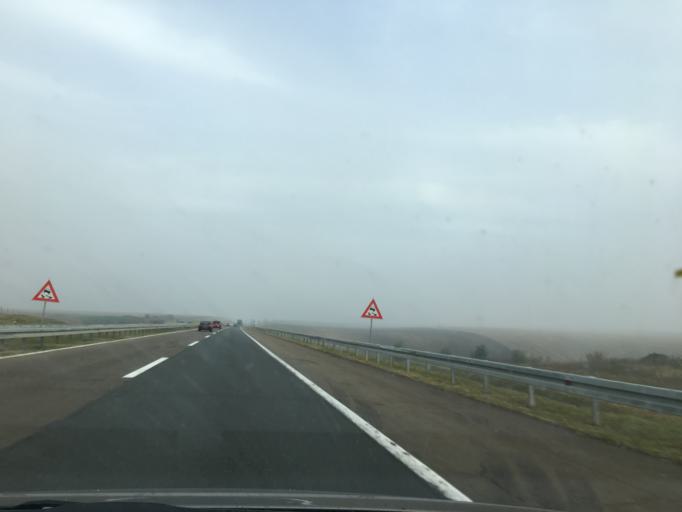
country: RS
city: Beska
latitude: 45.1167
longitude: 20.0987
